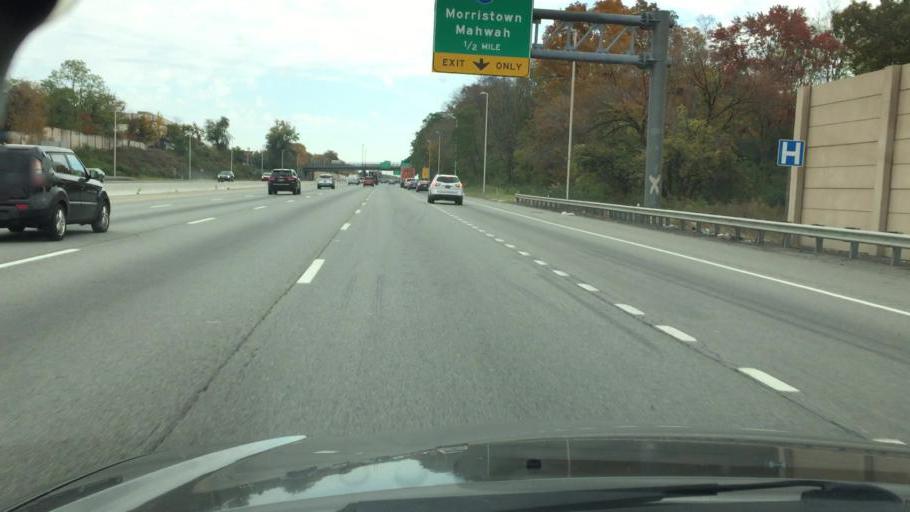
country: US
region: New Jersey
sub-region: Morris County
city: Parsippany
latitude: 40.8654
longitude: -74.4289
